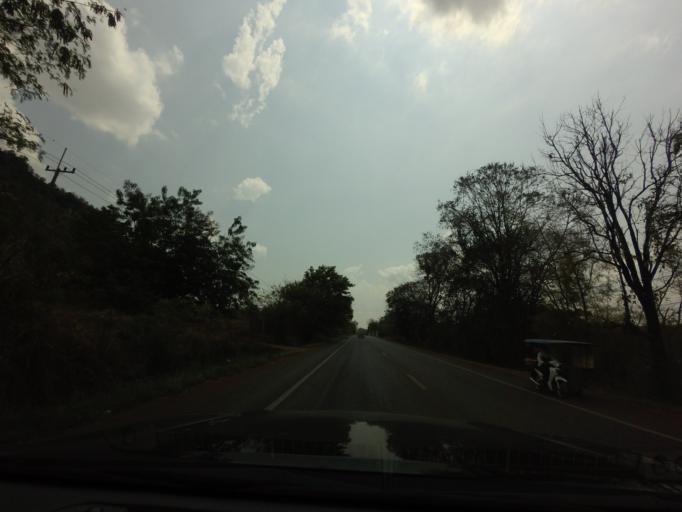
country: TH
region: Kanchanaburi
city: Sai Yok
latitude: 14.1443
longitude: 99.1462
